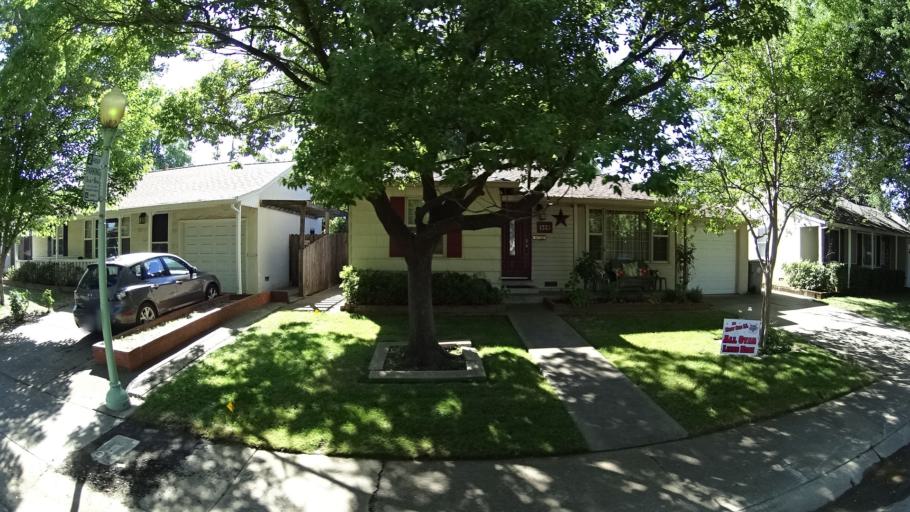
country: US
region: California
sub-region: Sacramento County
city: Florin
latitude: 38.5572
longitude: -121.4295
